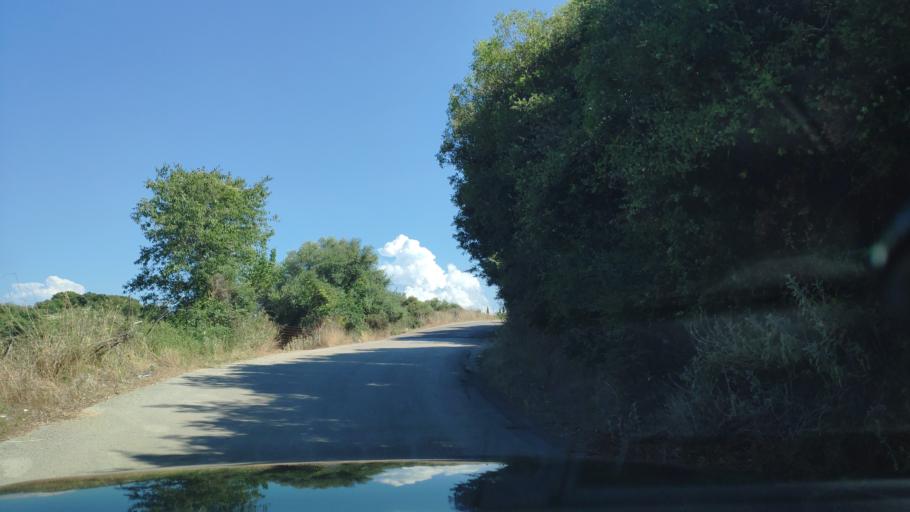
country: GR
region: West Greece
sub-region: Nomos Aitolias kai Akarnanias
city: Katouna
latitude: 38.7941
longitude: 21.1149
